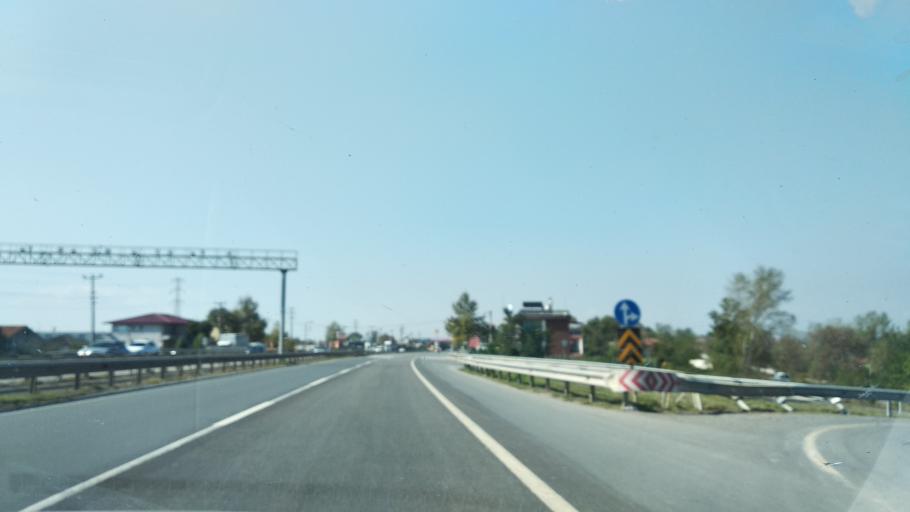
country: TR
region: Kocaeli
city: Derbent
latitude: 40.7297
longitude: 30.1398
